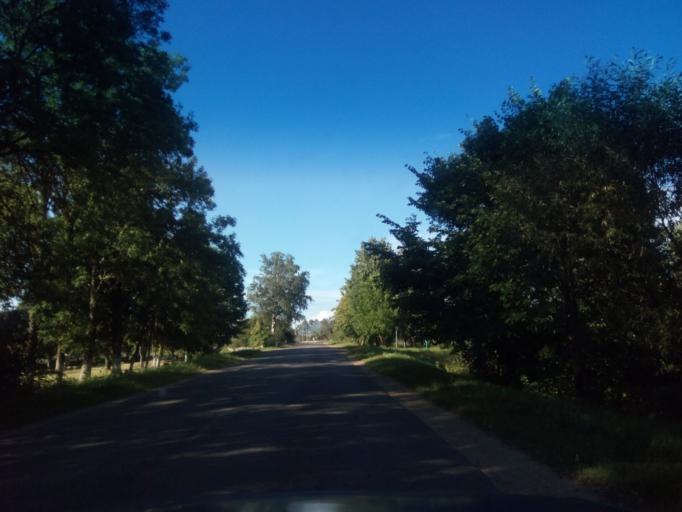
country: BY
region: Vitebsk
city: Dzisna
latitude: 55.6640
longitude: 28.3258
